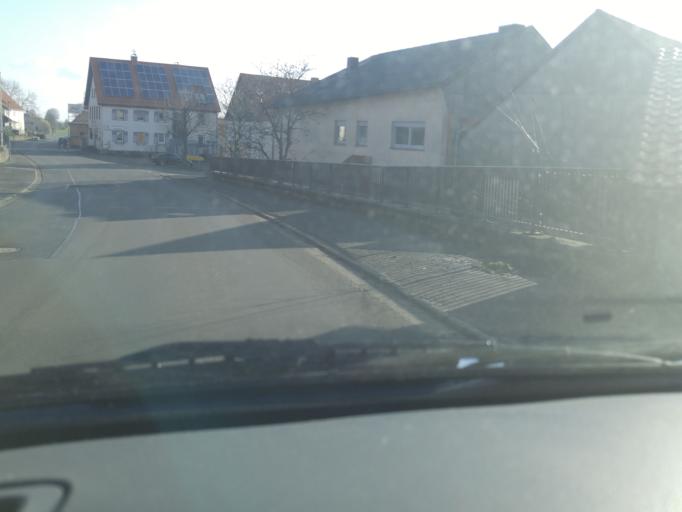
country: DE
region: Hesse
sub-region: Regierungsbezirk Giessen
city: Lautertal
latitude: 50.5806
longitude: 9.2624
